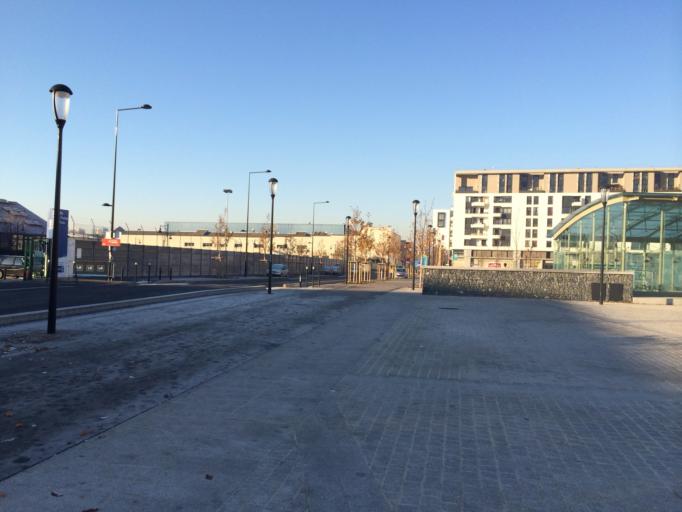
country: FR
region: Ile-de-France
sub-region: Departement de Seine-Saint-Denis
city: Aubervilliers
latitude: 48.9065
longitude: 2.3663
